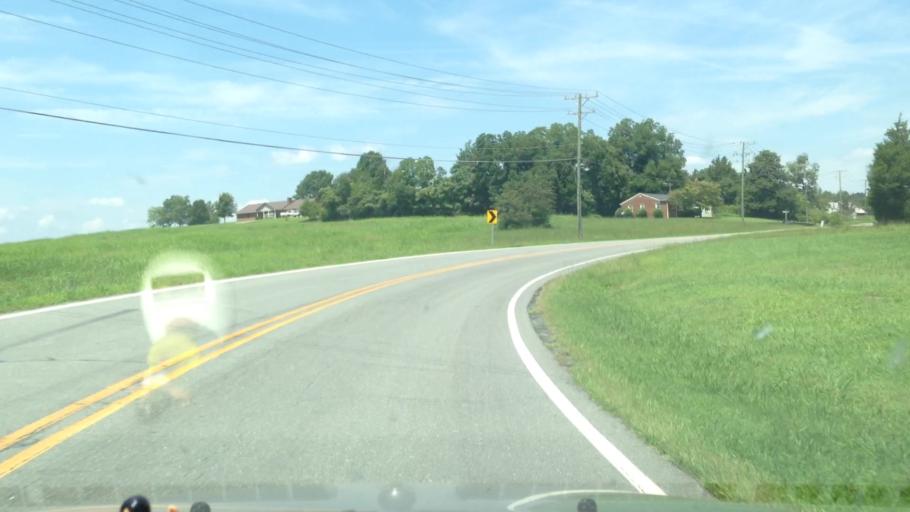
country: US
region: North Carolina
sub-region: Guilford County
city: Oak Ridge
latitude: 36.1929
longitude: -80.0601
